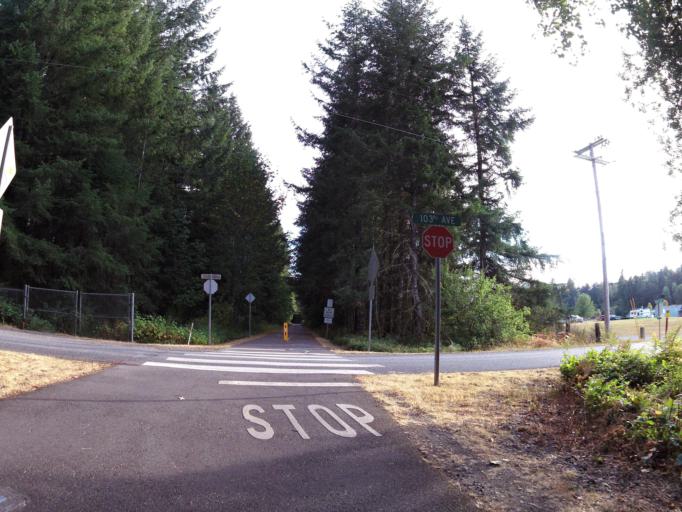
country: US
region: Washington
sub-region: Thurston County
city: Tenino
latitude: 46.9384
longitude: -122.8226
